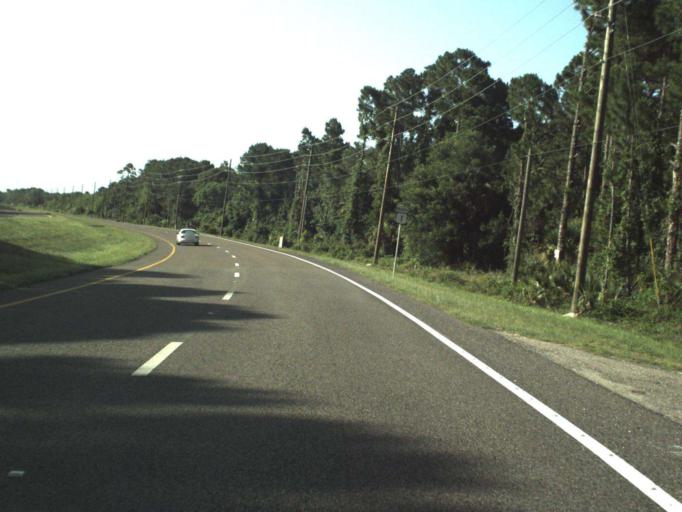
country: US
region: Florida
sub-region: Volusia County
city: Oak Hill
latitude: 28.8343
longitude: -80.8416
